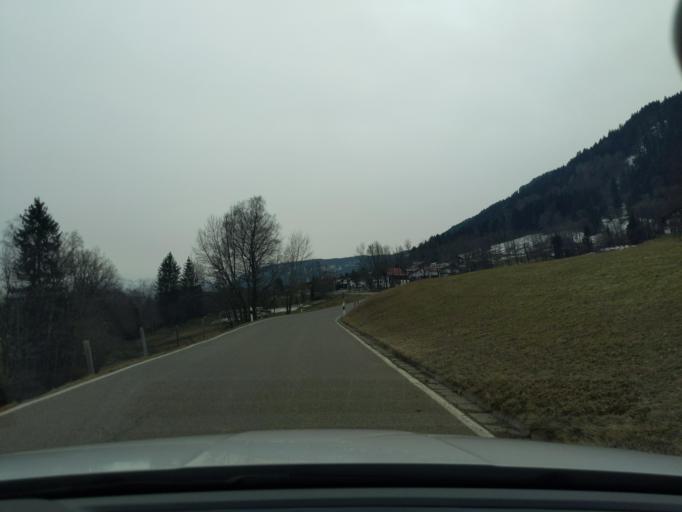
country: DE
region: Bavaria
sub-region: Swabia
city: Bolsterlang
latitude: 47.4780
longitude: 10.2319
